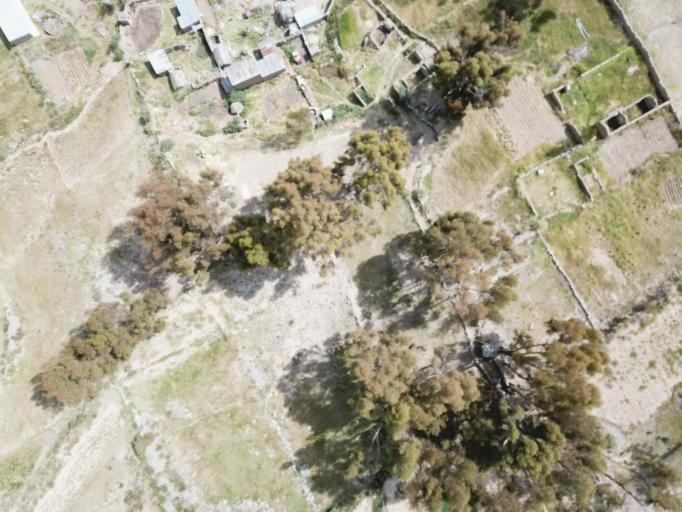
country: BO
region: La Paz
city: Achacachi
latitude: -16.0542
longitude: -68.8103
